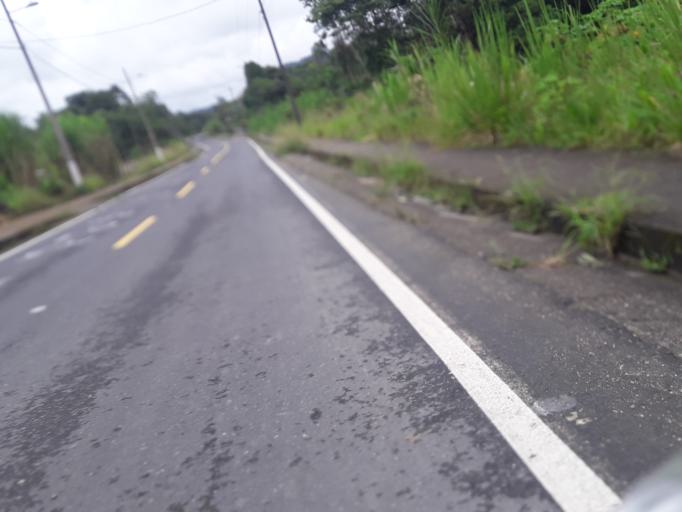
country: EC
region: Napo
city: Tena
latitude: -0.9603
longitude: -77.8590
